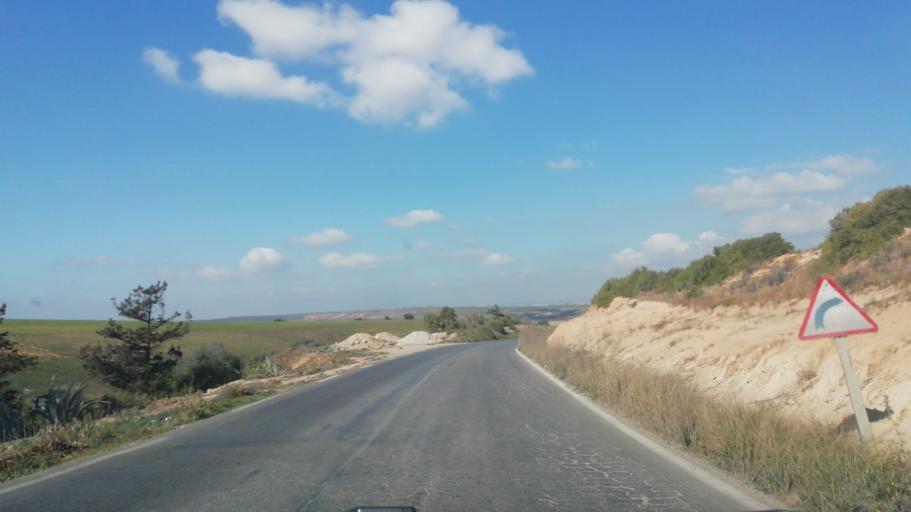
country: DZ
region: Oran
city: Ain el Bya
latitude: 35.7281
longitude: -0.2489
